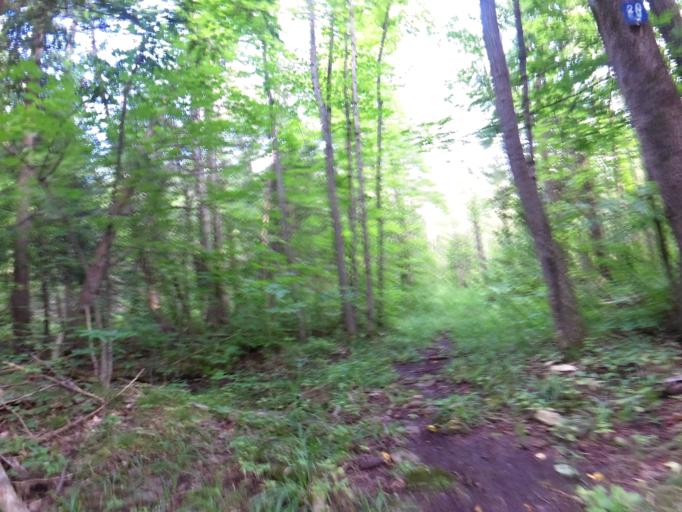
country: CA
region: Ontario
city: Bells Corners
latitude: 45.3229
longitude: -75.8590
